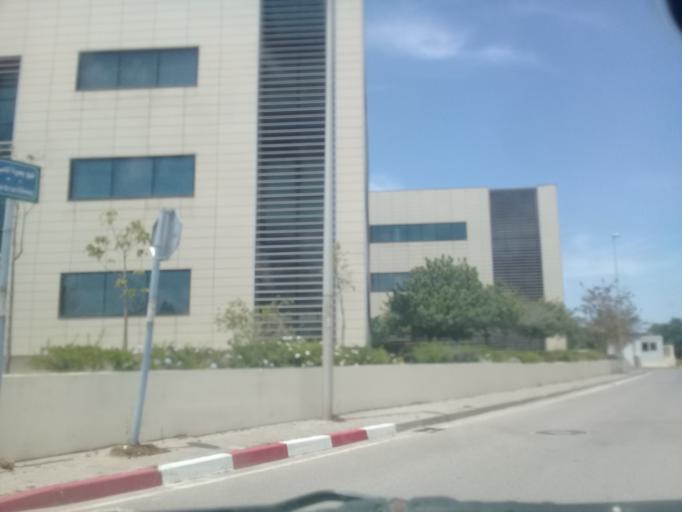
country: TN
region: Ariana
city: Ariana
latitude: 36.8351
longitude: 10.2274
